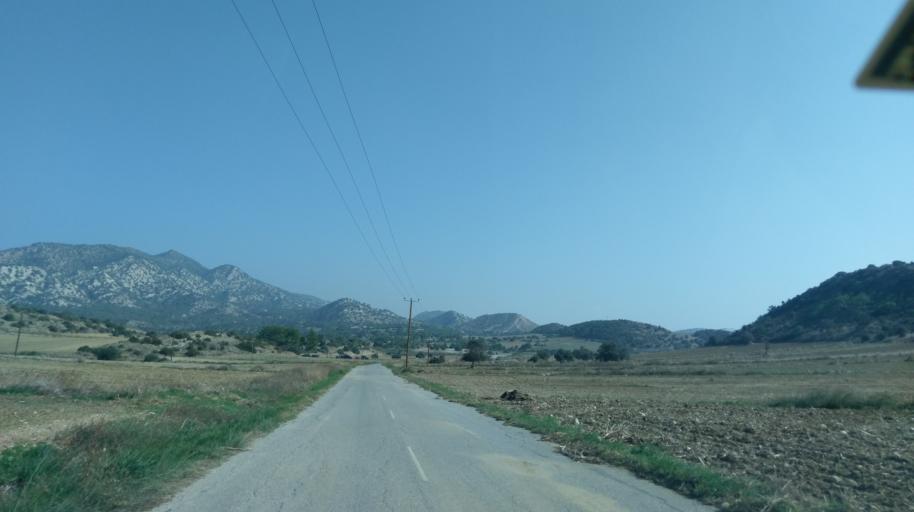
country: CY
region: Ammochostos
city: Lefkonoiko
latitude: 35.3307
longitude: 33.7141
